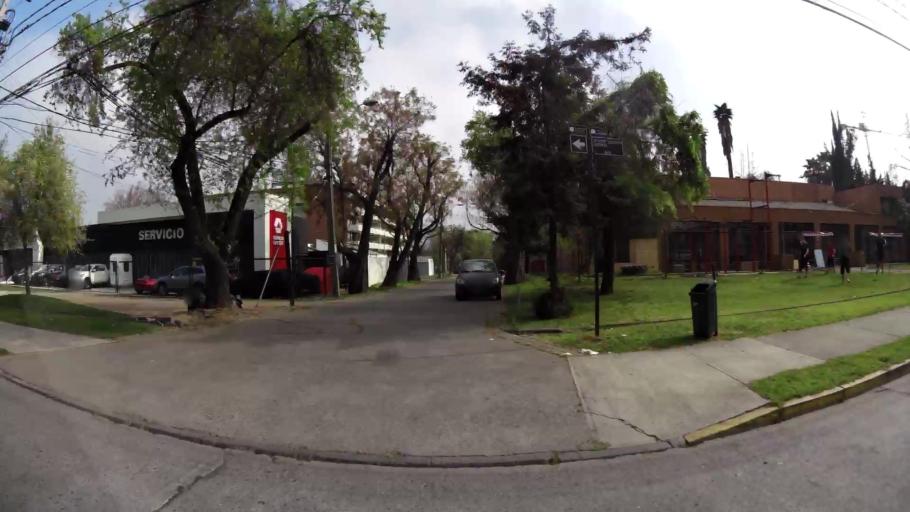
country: CL
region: Santiago Metropolitan
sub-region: Provincia de Santiago
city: Villa Presidente Frei, Nunoa, Santiago, Chile
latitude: -33.3875
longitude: -70.5429
